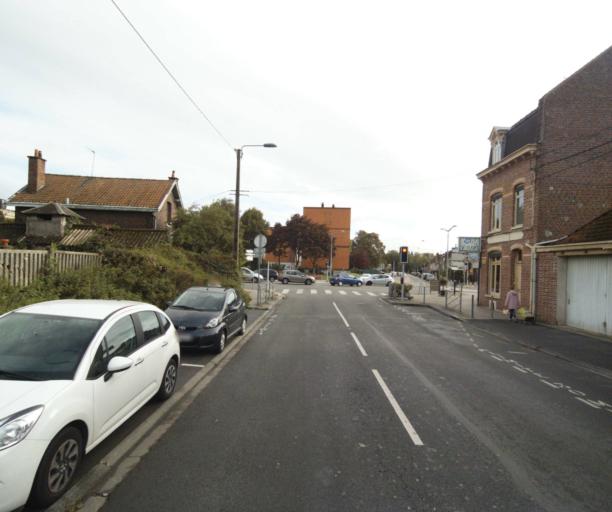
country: FR
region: Nord-Pas-de-Calais
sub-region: Departement du Nord
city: Lambersart
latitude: 50.6444
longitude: 3.0128
